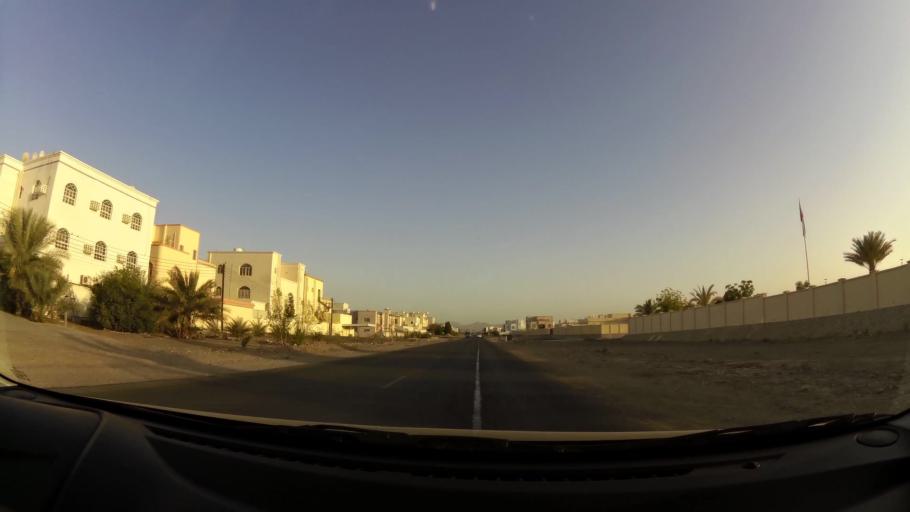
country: OM
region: Muhafazat Masqat
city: As Sib al Jadidah
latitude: 23.6152
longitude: 58.1942
